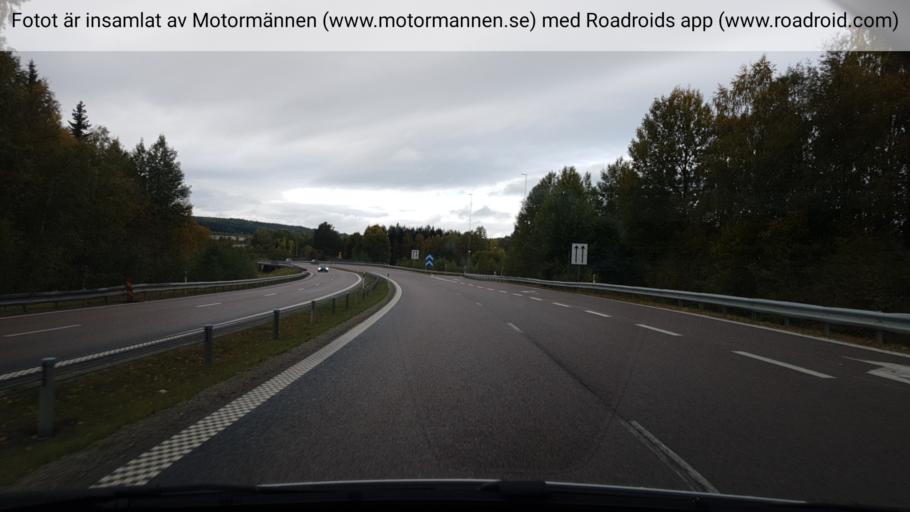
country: SE
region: Vaesternorrland
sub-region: OErnskoeldsviks Kommun
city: Ornskoldsvik
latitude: 63.3162
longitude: 18.7981
